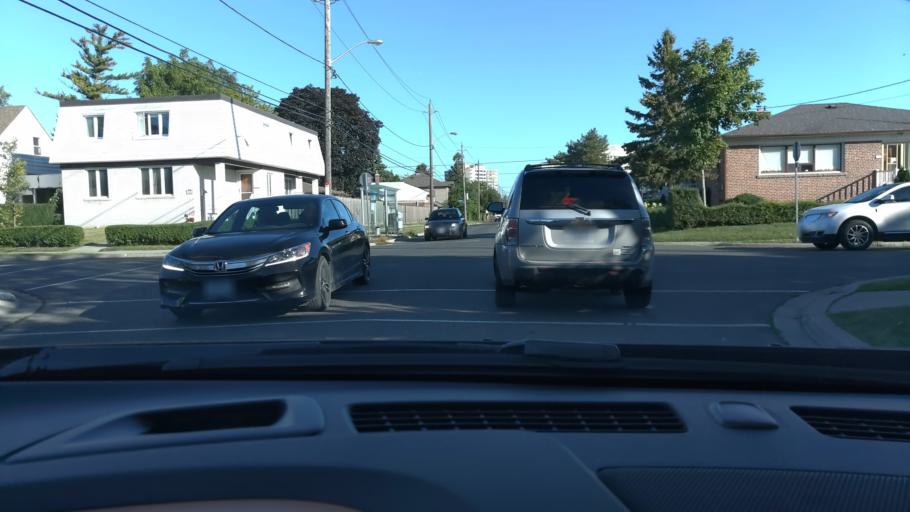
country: CA
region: Ontario
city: Toronto
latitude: 43.7249
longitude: -79.4393
